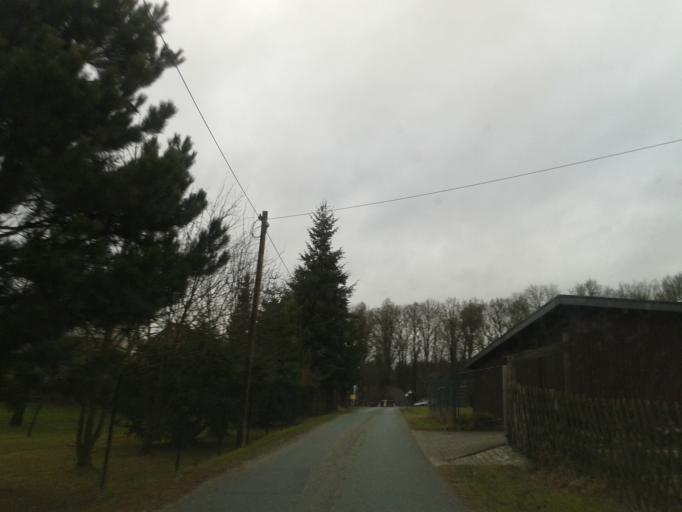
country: DE
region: Saxony
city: Neugersdorf
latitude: 50.9625
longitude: 14.6207
